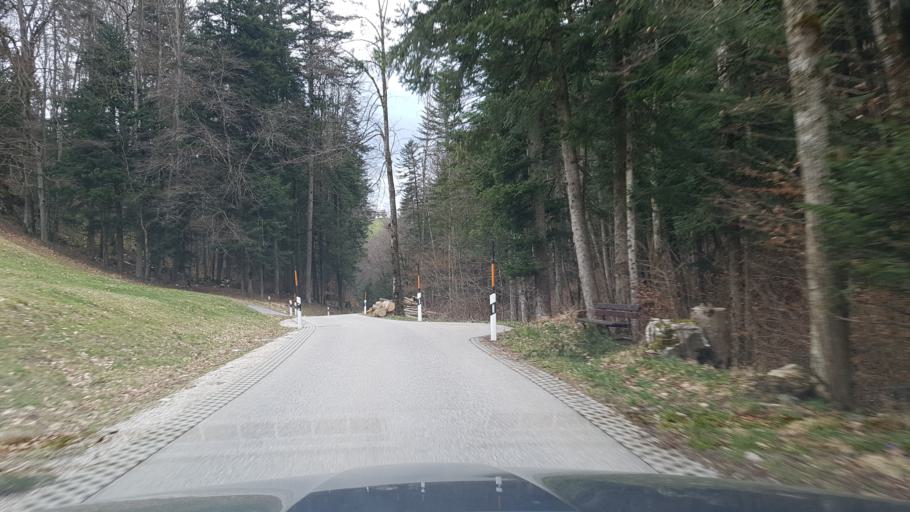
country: DE
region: Bavaria
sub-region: Upper Bavaria
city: Marktschellenberg
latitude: 47.6826
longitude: 13.0631
